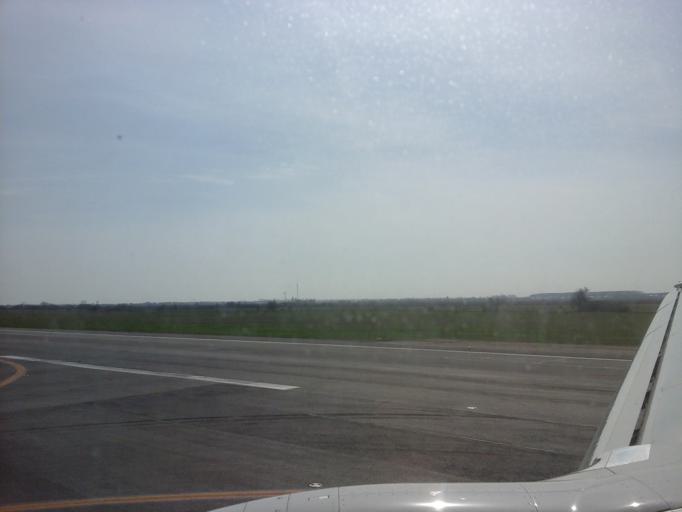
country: RO
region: Ilfov
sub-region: Comuna Otopeni
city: Otopeni
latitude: 44.5673
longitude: 26.1078
